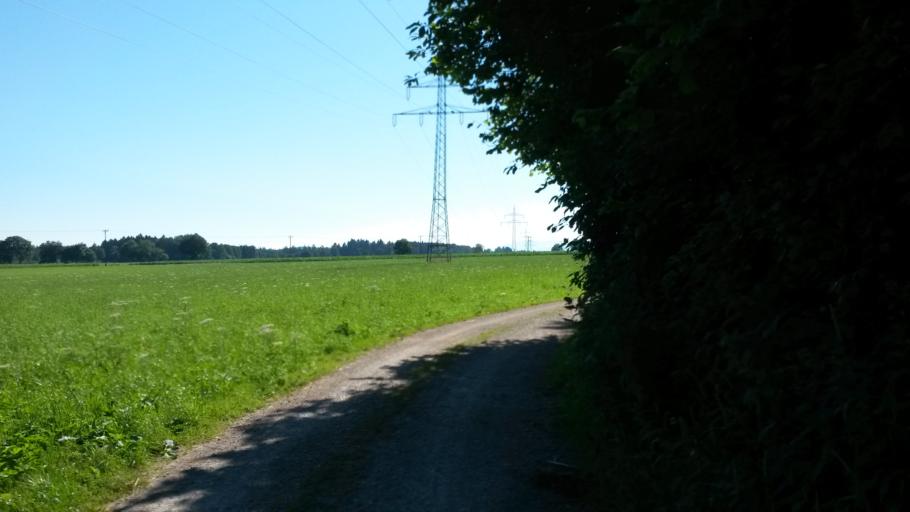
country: DE
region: Bavaria
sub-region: Upper Bavaria
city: Bernau am Chiemsee
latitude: 47.7996
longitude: 12.4006
